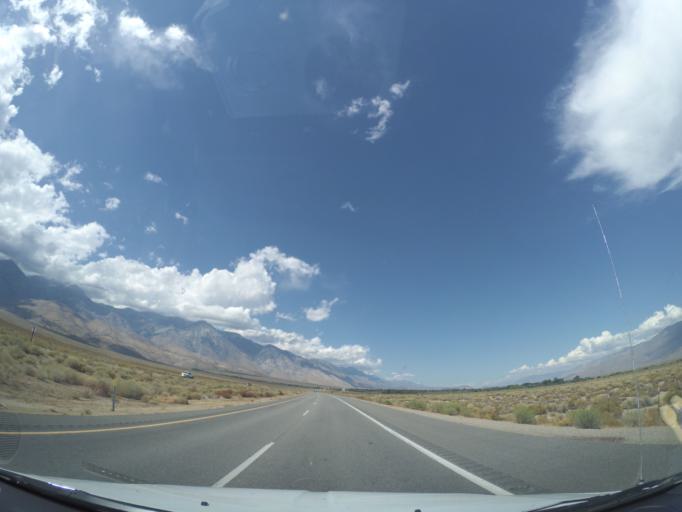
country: US
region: California
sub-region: Inyo County
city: Lone Pine
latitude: 36.8154
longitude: -118.2083
